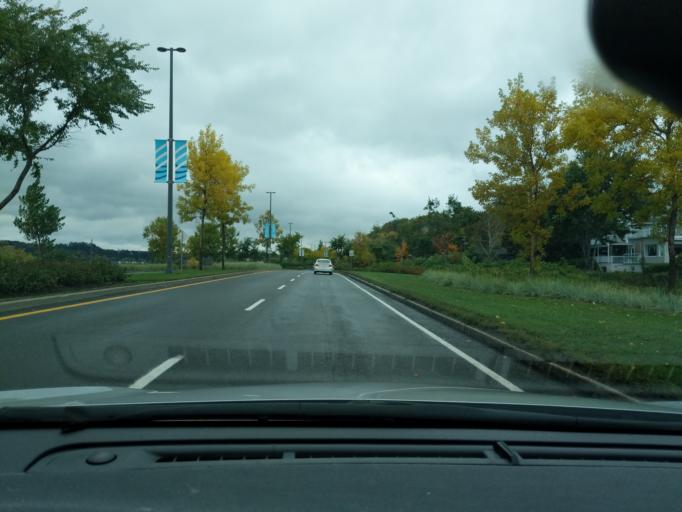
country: CA
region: Quebec
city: Quebec
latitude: 46.7613
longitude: -71.2653
